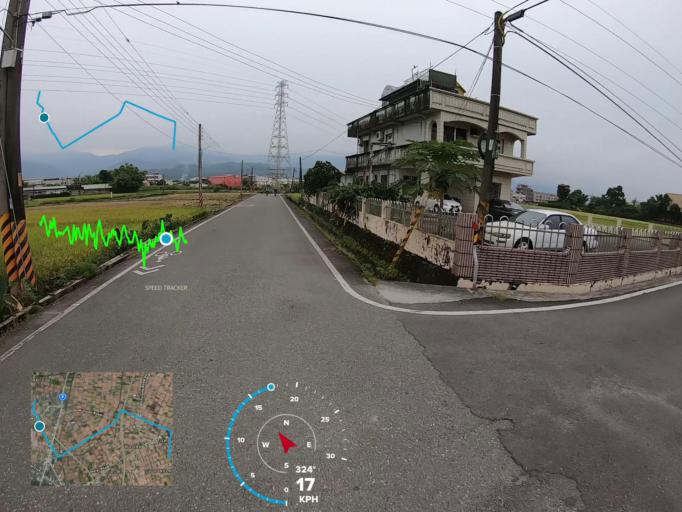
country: TW
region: Taiwan
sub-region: Yilan
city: Yilan
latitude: 24.7807
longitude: 121.7631
